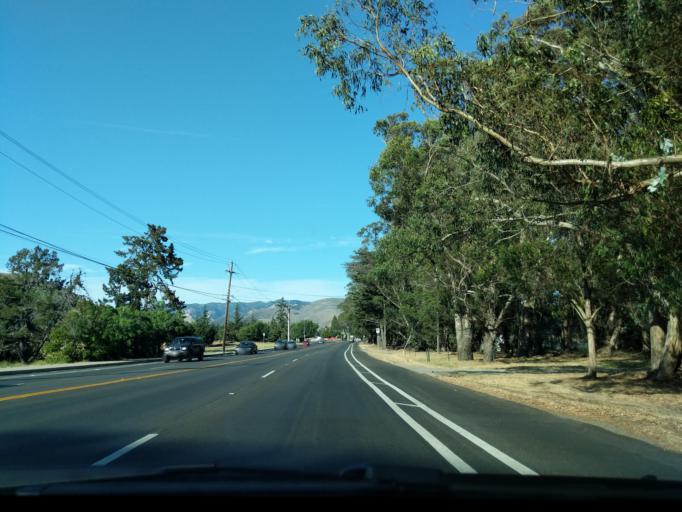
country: US
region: California
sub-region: San Luis Obispo County
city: San Luis Obispo
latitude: 35.2598
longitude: -120.6833
